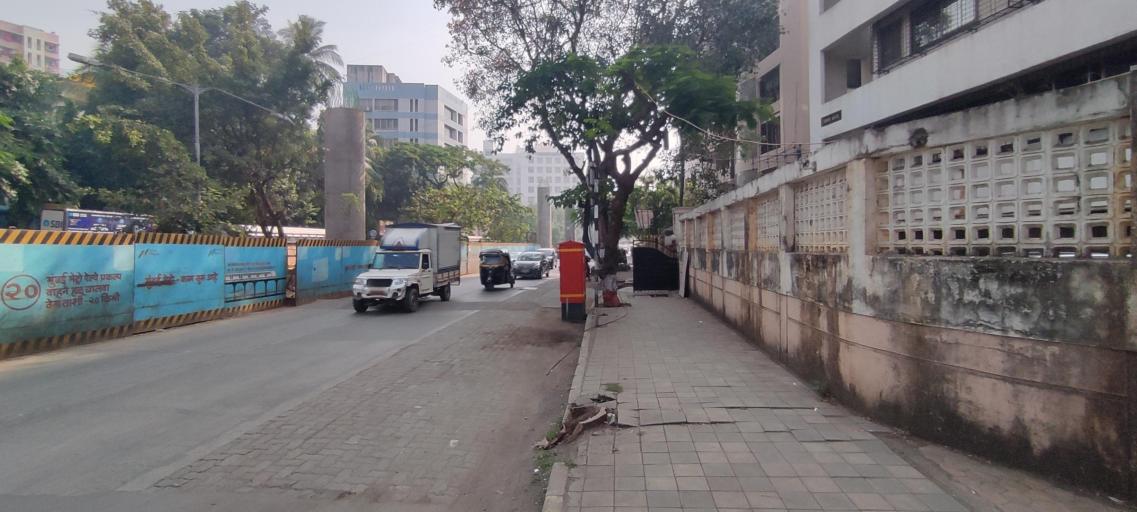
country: IN
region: Maharashtra
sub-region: Mumbai Suburban
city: Mumbai
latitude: 19.1120
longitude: 72.8372
